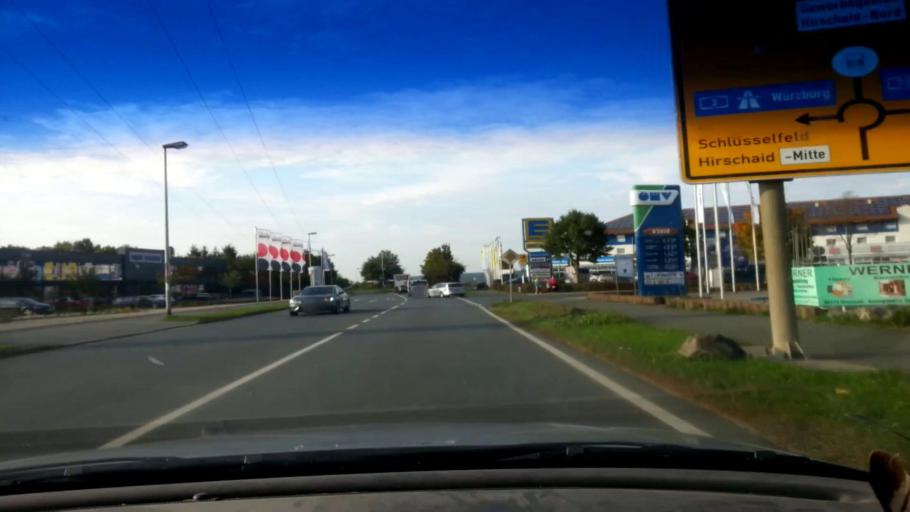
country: DE
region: Bavaria
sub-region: Upper Franconia
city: Hirschaid
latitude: 49.8195
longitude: 11.0007
